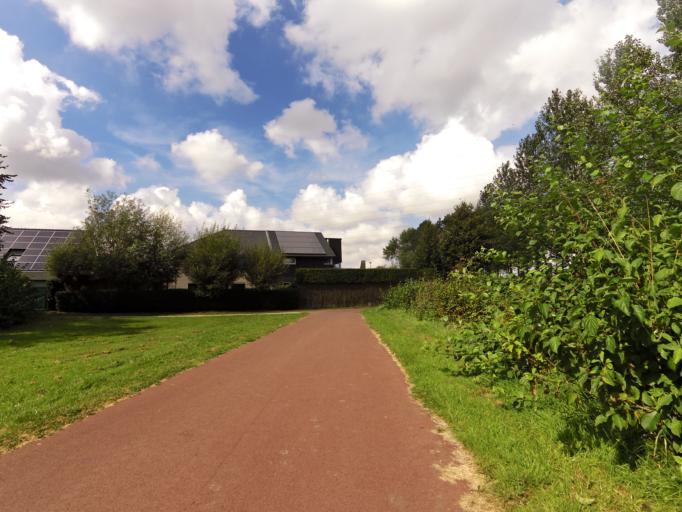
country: BE
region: Flanders
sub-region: Provincie West-Vlaanderen
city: Sint-Kruis
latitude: 51.2331
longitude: 3.2480
